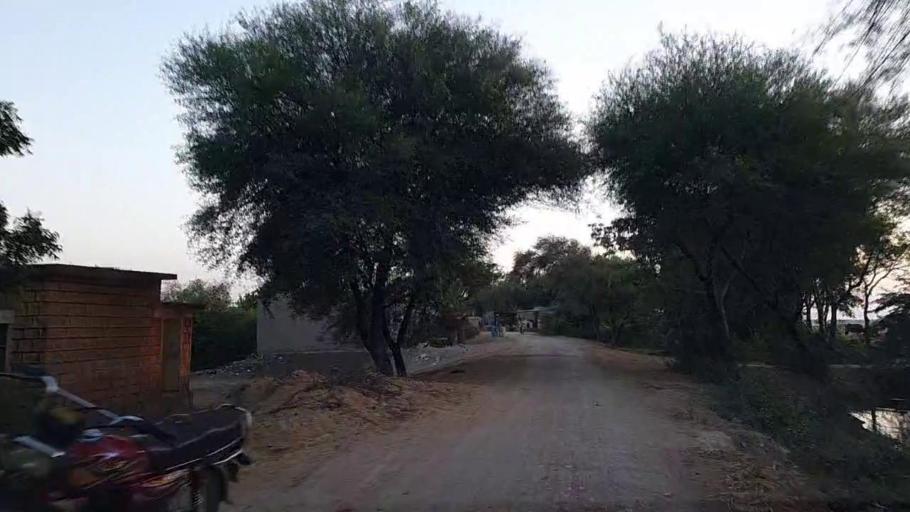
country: PK
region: Sindh
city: Mirpur Batoro
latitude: 24.6133
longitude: 68.1843
